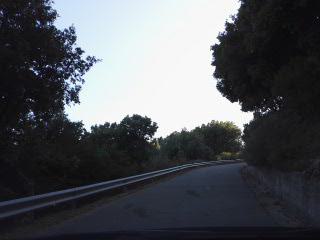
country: IT
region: Calabria
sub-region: Provincia di Vibo-Valentia
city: Nardodipace
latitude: 38.4294
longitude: 16.3415
